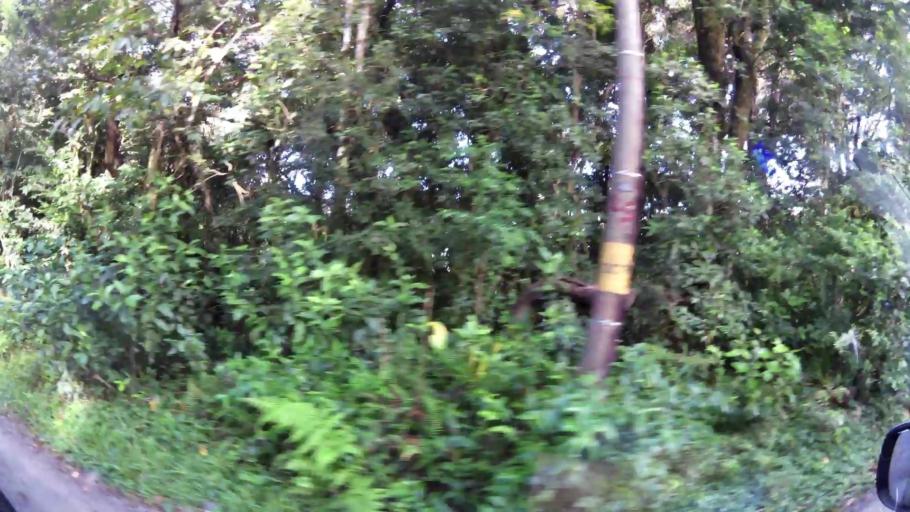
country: CR
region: Guanacaste
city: Juntas
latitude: 10.3014
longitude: -84.8017
